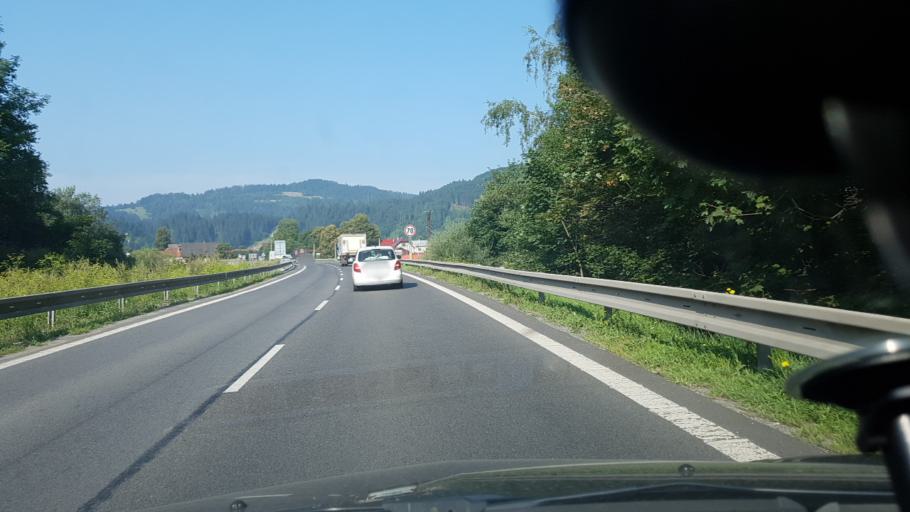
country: SK
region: Zilinsky
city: Tvrdosin
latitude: 49.3093
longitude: 19.4926
